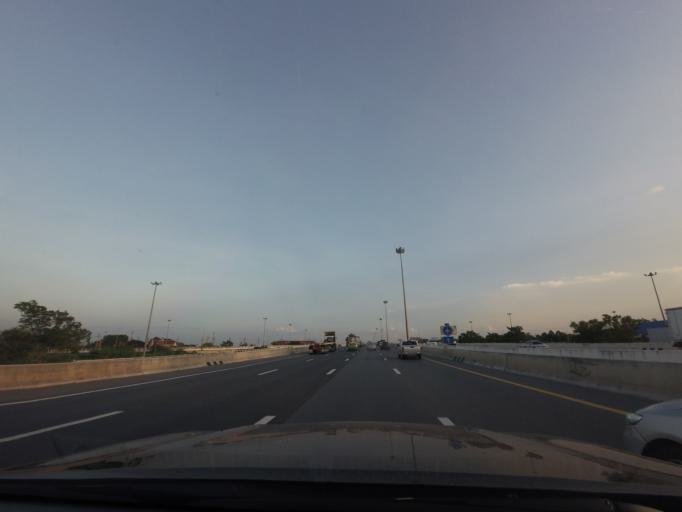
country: TH
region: Pathum Thani
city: Thanyaburi
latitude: 14.0100
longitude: 100.7041
